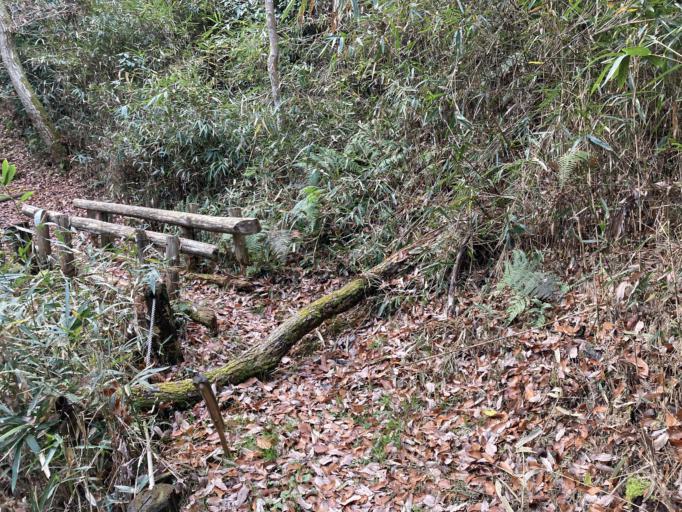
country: JP
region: Nara
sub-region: Ikoma-shi
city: Ikoma
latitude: 34.7010
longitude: 135.6779
